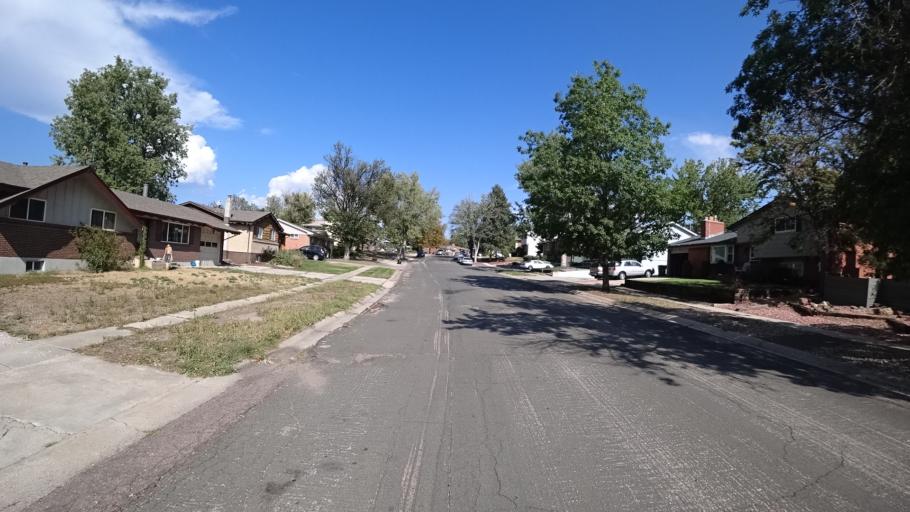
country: US
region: Colorado
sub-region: El Paso County
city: Colorado Springs
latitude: 38.8606
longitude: -104.7635
